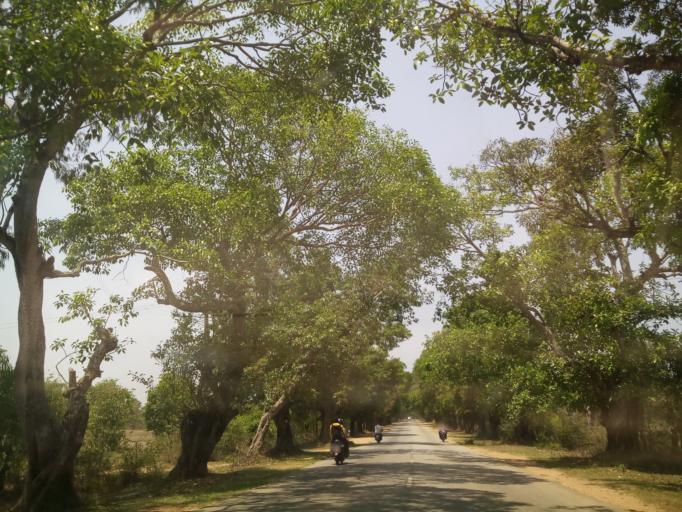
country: IN
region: Karnataka
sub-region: Hassan
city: Alur
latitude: 12.9475
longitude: 75.9560
